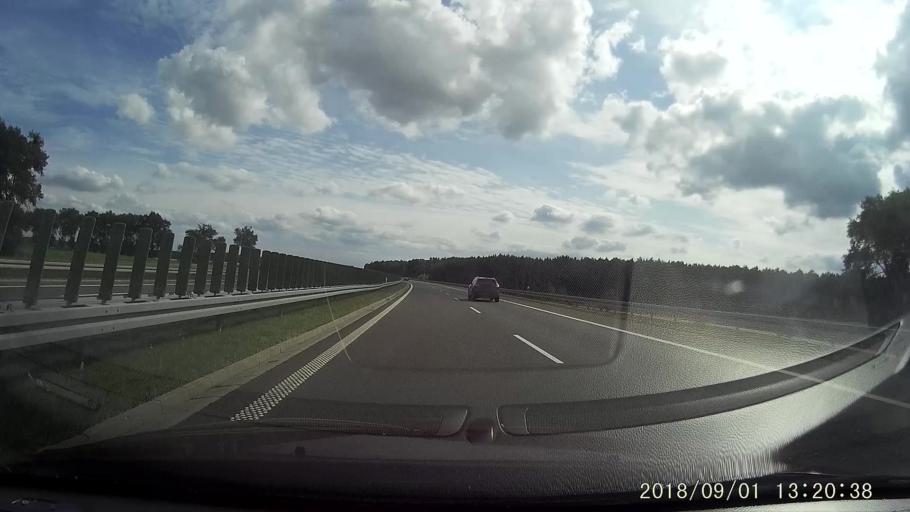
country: PL
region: West Pomeranian Voivodeship
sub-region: Powiat pyrzycki
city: Bielice
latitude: 53.1682
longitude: 14.6973
